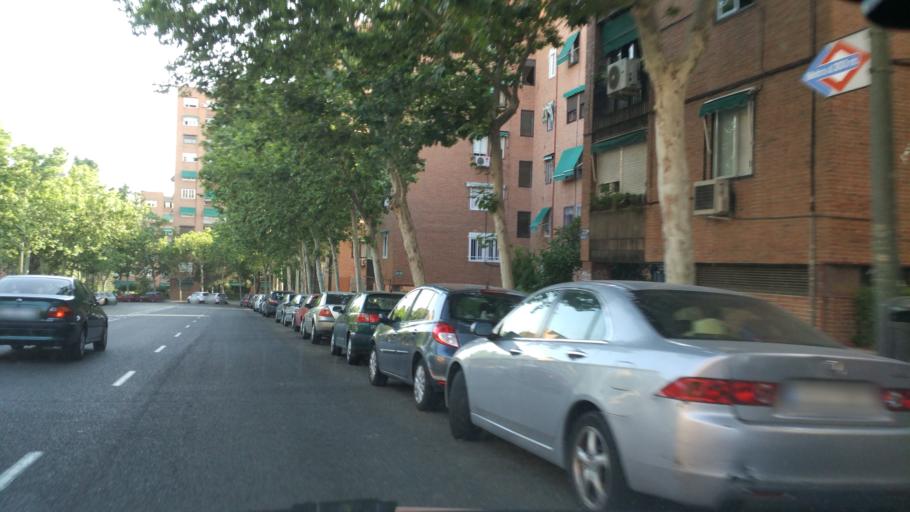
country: ES
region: Madrid
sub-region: Provincia de Madrid
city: Tetuan de las Victorias
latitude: 40.4681
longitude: -3.7194
